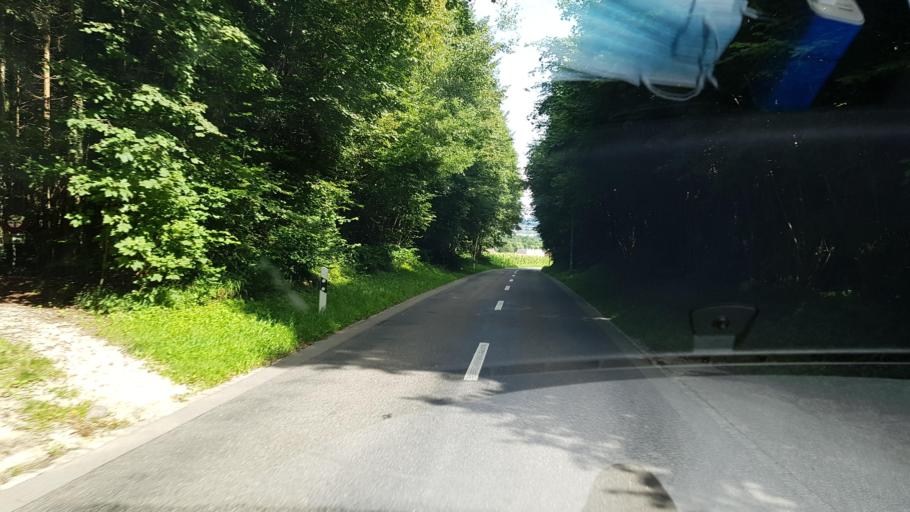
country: CH
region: Bern
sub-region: Oberaargau
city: Attiswil
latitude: 47.2424
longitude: 7.5922
